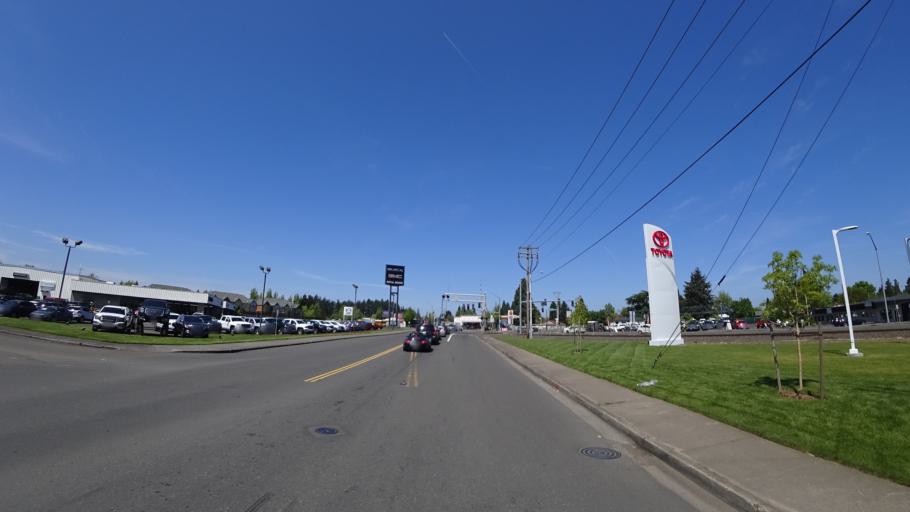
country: US
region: Oregon
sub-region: Washington County
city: Hillsboro
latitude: 45.5092
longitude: -122.9685
